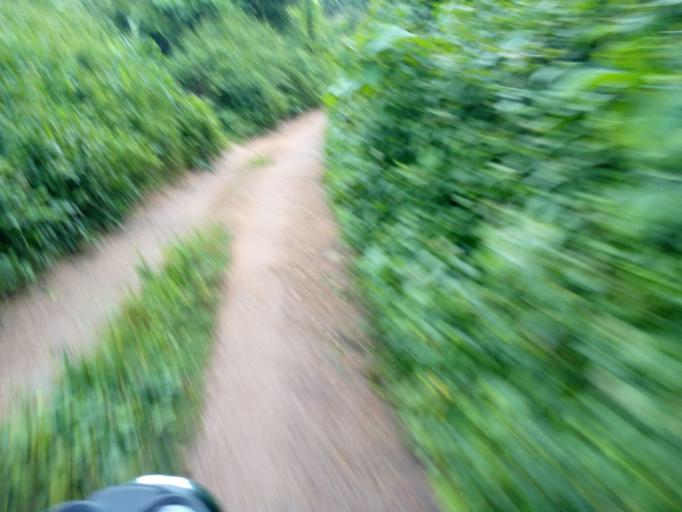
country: SL
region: Eastern Province
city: Buedu
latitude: 8.4711
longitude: -10.3489
